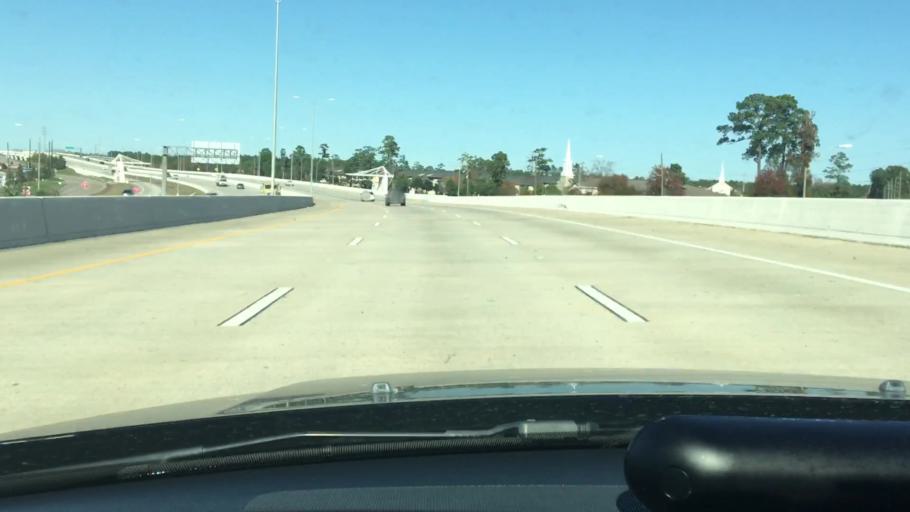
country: US
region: Texas
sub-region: Harris County
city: Atascocita
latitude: 29.9259
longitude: -95.2002
